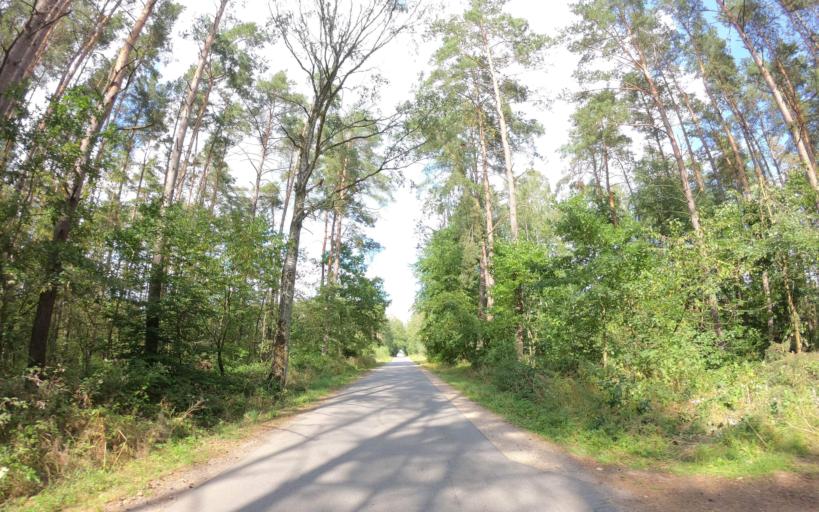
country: PL
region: West Pomeranian Voivodeship
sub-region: Powiat drawski
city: Wierzchowo
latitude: 53.4508
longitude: 16.0819
